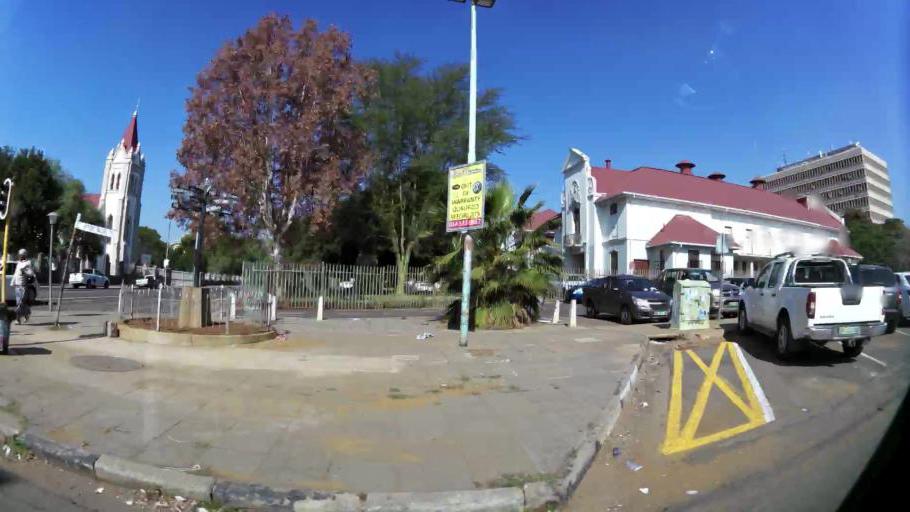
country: ZA
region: North-West
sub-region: Bojanala Platinum District Municipality
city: Rustenburg
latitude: -25.6717
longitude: 27.2446
